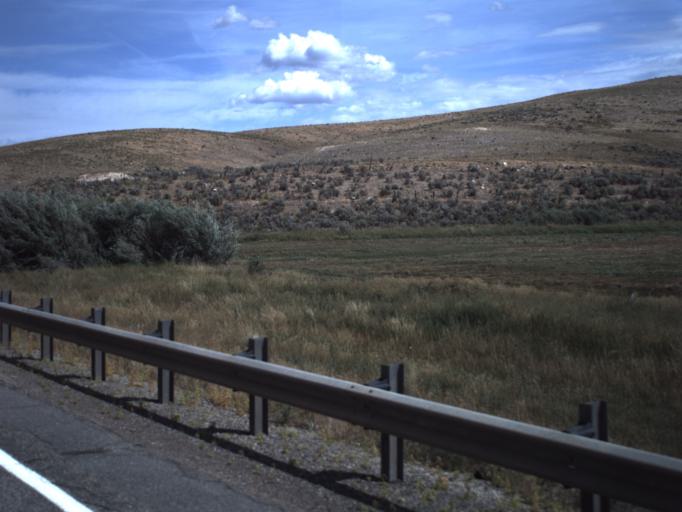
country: US
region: Utah
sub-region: Sanpete County
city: Fairview
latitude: 39.8126
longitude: -111.5059
